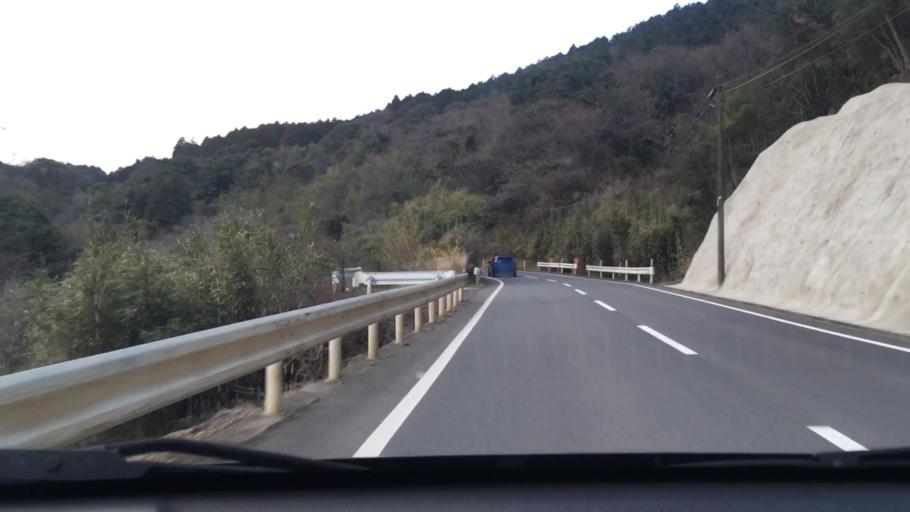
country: JP
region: Oita
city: Hiji
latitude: 33.3697
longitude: 131.4658
